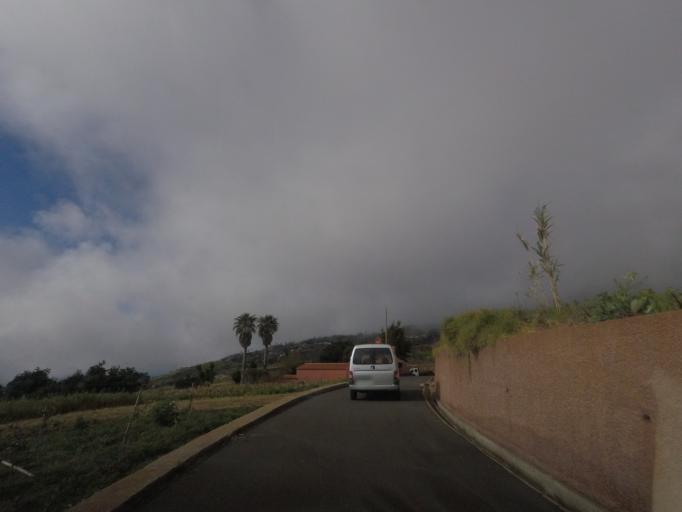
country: PT
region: Madeira
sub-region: Calheta
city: Faja da Ovelha
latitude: 32.7664
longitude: -17.2216
